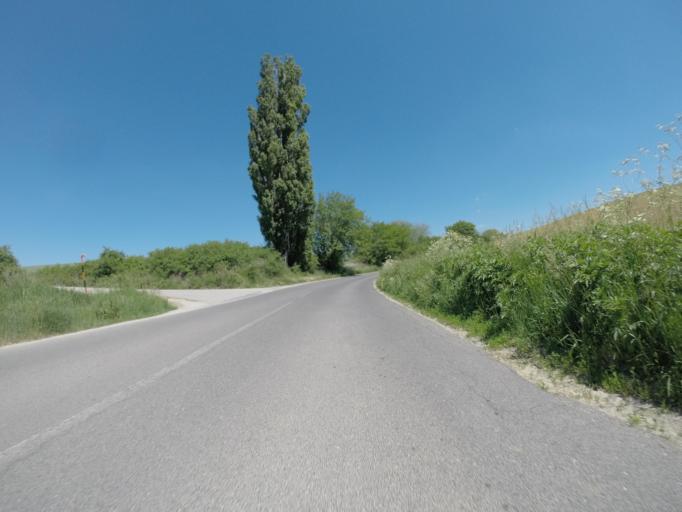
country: SK
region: Trnavsky
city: Hlohovec
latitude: 48.4605
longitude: 17.8456
